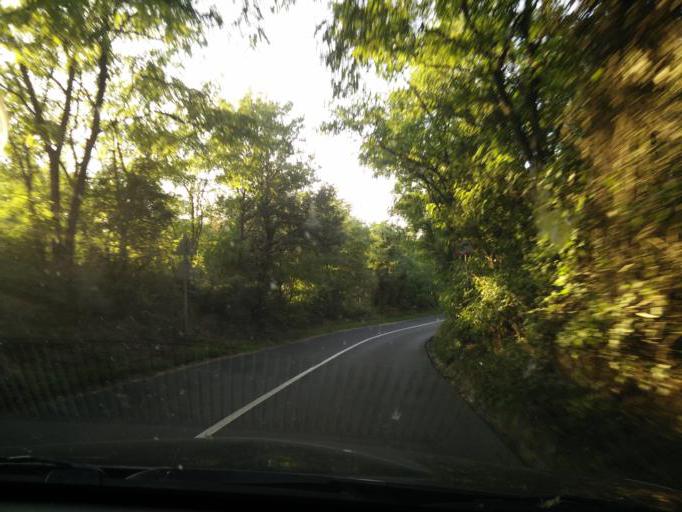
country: HU
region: Pest
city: Perbal
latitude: 47.6332
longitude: 18.7797
